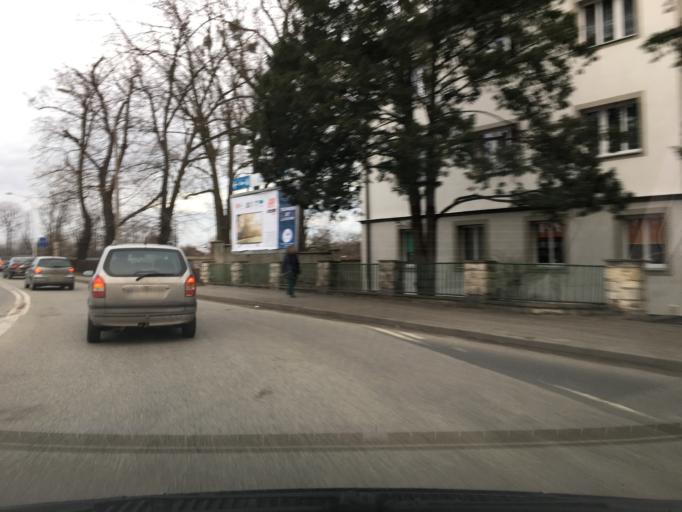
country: PL
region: Opole Voivodeship
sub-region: Powiat kedzierzynsko-kozielski
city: Kozle
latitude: 50.3351
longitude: 18.1476
